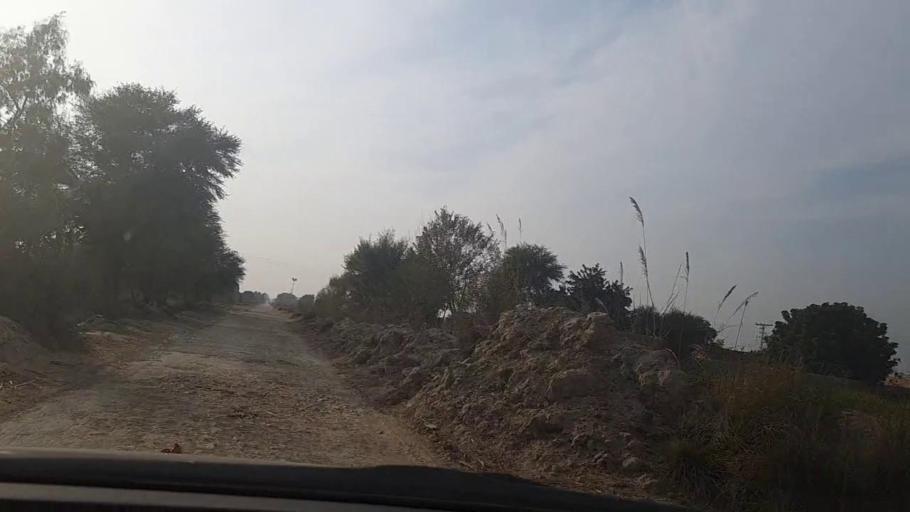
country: PK
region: Sindh
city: Daulatpur
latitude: 26.3340
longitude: 68.0745
